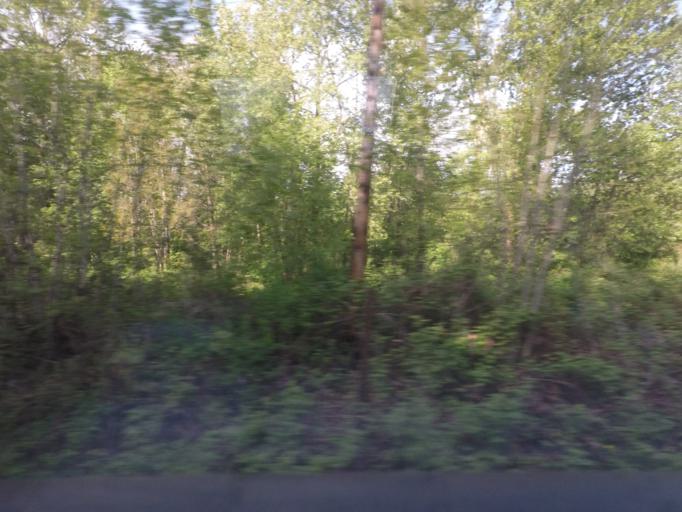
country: CA
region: British Columbia
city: New Westminster
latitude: 49.2485
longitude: -122.9086
